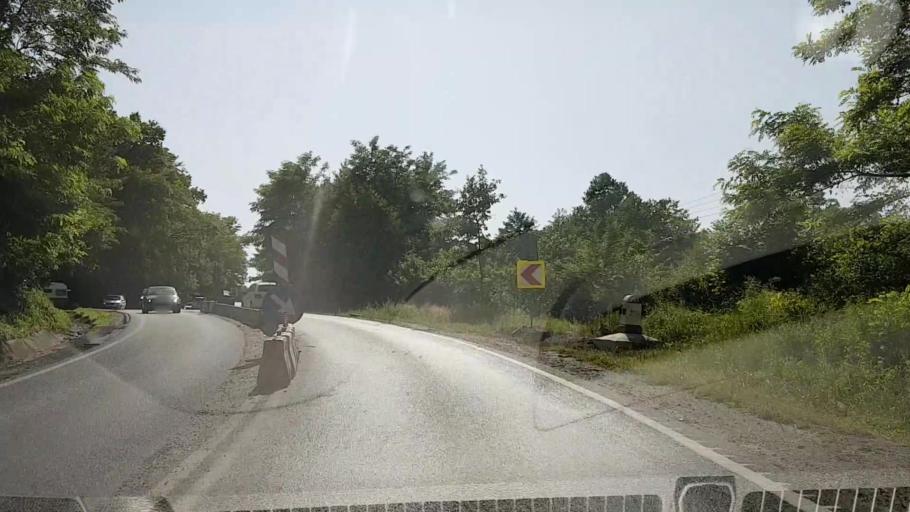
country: RO
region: Sibiu
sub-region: Comuna Talmaciu
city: Talmaciu
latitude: 45.7029
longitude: 24.2809
